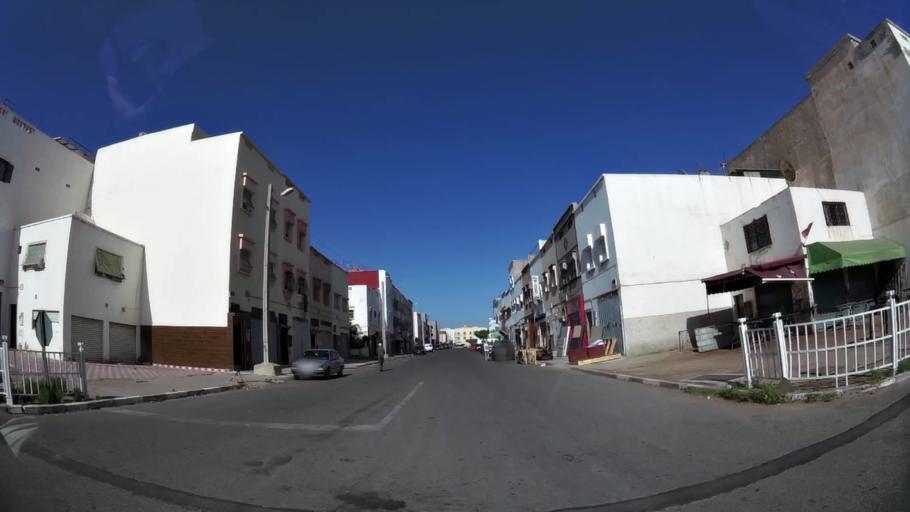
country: MA
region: Oued ed Dahab-Lagouira
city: Dakhla
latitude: 30.4090
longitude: -9.5671
